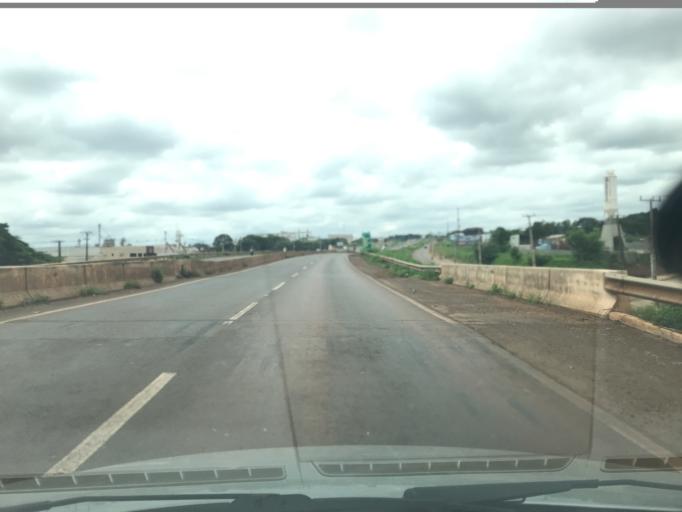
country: BR
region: Parana
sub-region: Paicandu
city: Paicandu
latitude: -23.4466
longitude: -51.9976
